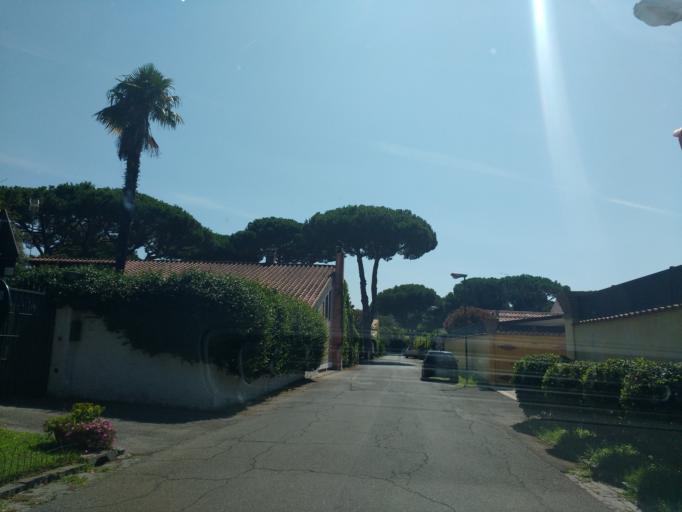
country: IT
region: Latium
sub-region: Citta metropolitana di Roma Capitale
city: Acilia-Castel Fusano-Ostia Antica
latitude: 41.7497
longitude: 12.3593
